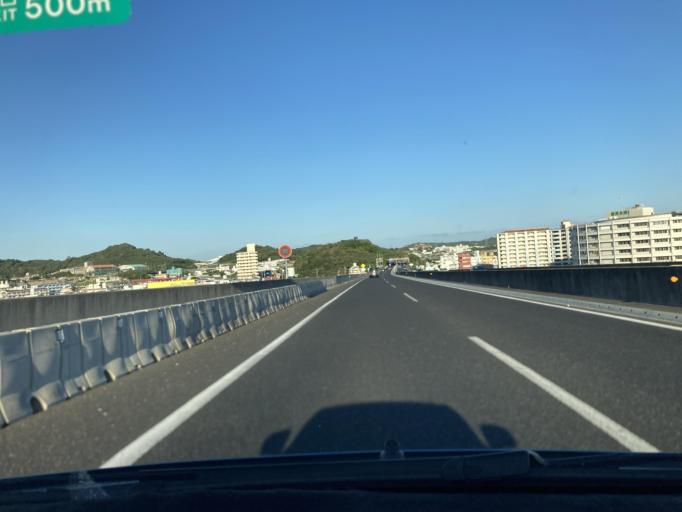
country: JP
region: Okinawa
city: Tomigusuku
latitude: 26.1785
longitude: 127.7126
